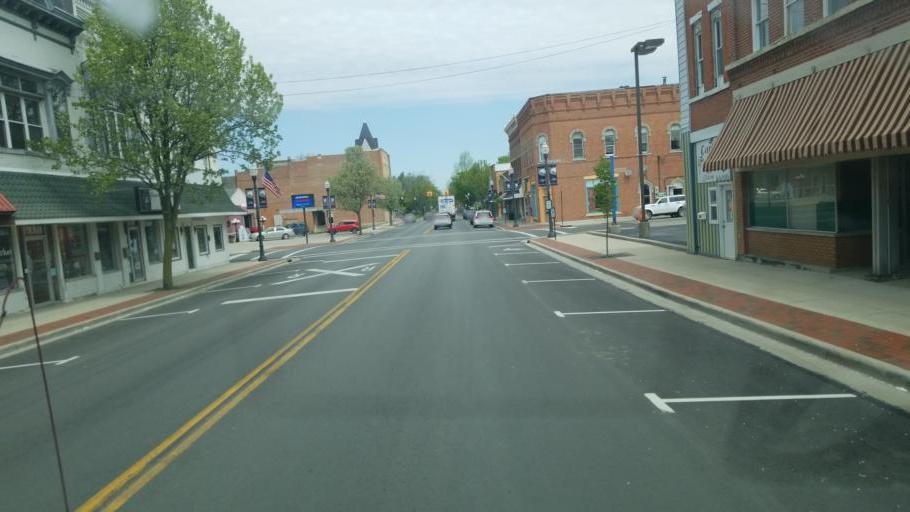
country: US
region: Ohio
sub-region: Hardin County
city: Ada
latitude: 40.7709
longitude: -83.8232
